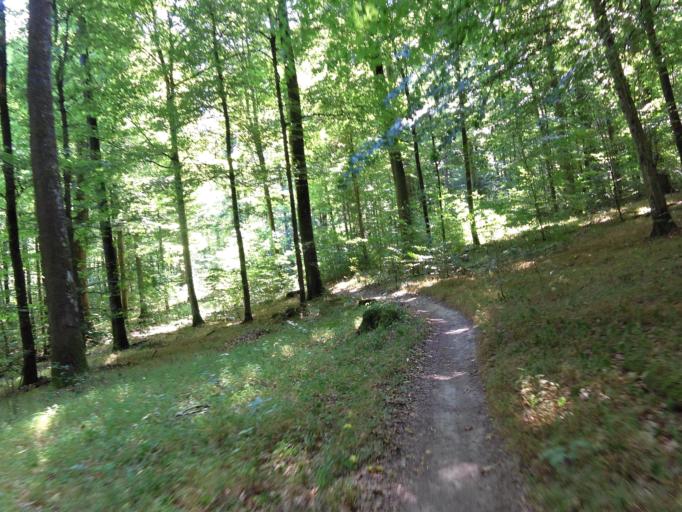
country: DE
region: Bavaria
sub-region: Regierungsbezirk Unterfranken
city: Wuerzburg
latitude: 49.7542
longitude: 9.8832
